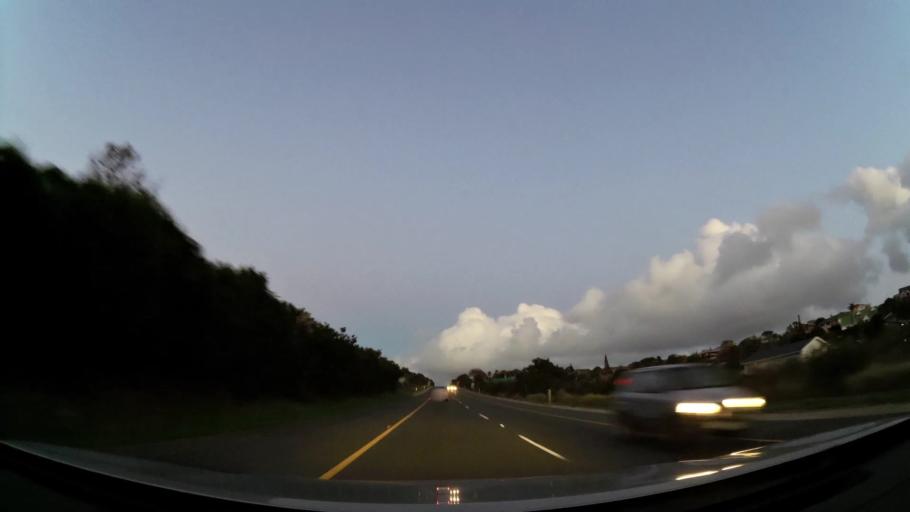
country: ZA
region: Western Cape
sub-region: Eden District Municipality
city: Knysna
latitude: -34.0200
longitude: 22.8208
